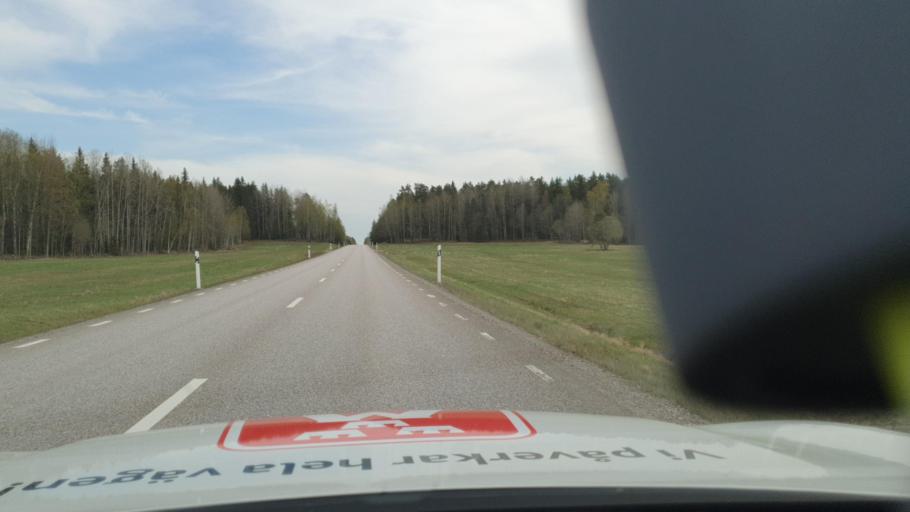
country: SE
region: Uppsala
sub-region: Heby Kommun
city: Heby
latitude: 59.9157
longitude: 16.8867
